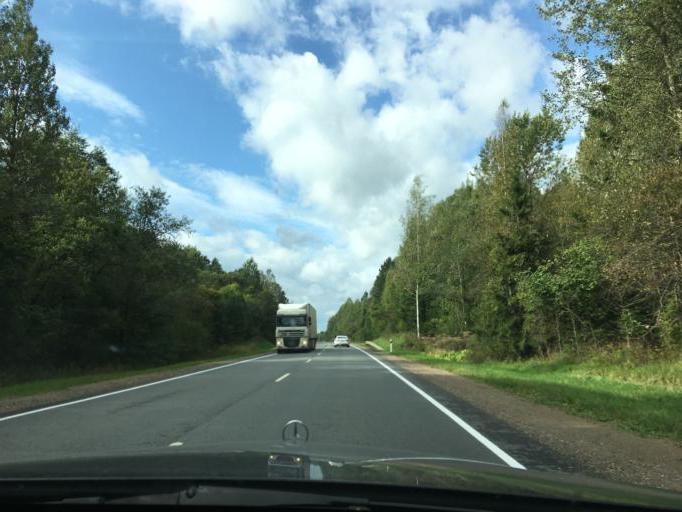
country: RU
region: Tverskaya
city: Toropets
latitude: 56.3406
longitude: 31.3320
